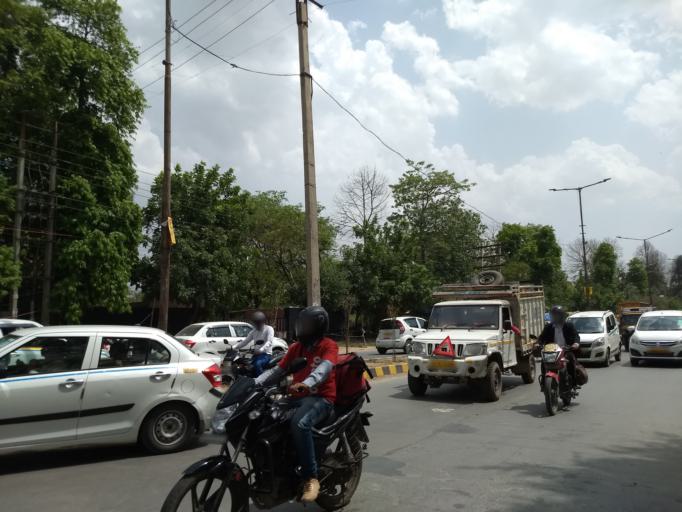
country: IN
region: Haryana
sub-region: Gurgaon
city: Gurgaon
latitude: 28.5106
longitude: 77.0739
